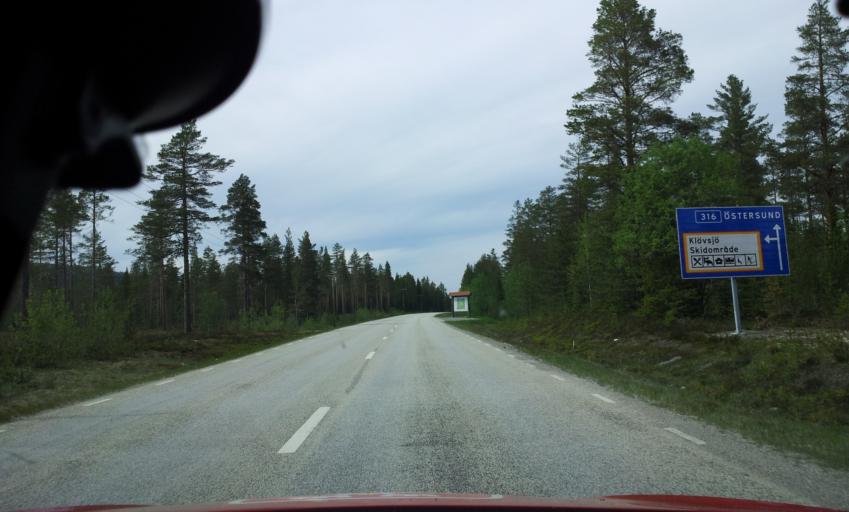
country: SE
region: Jaemtland
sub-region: Bergs Kommun
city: Hoverberg
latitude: 62.5013
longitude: 14.2039
